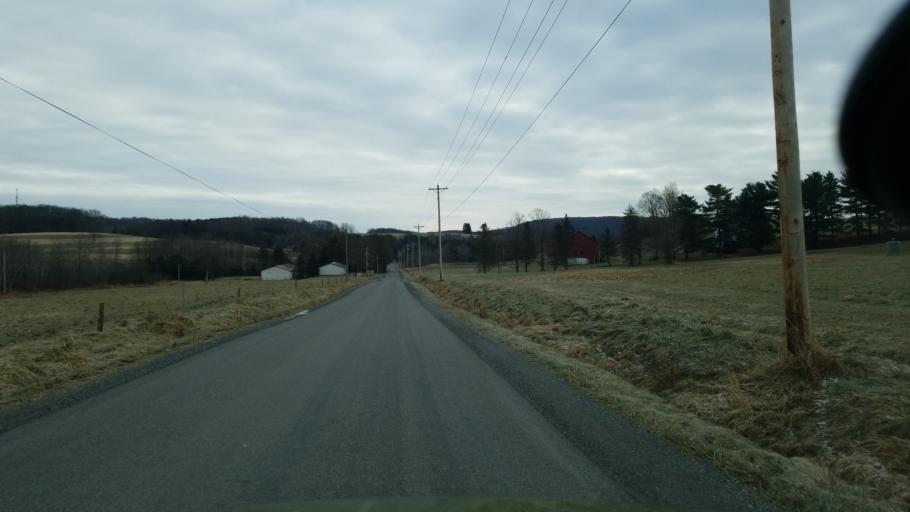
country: US
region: Pennsylvania
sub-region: Clearfield County
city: Treasure Lake
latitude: 41.1107
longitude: -78.6576
